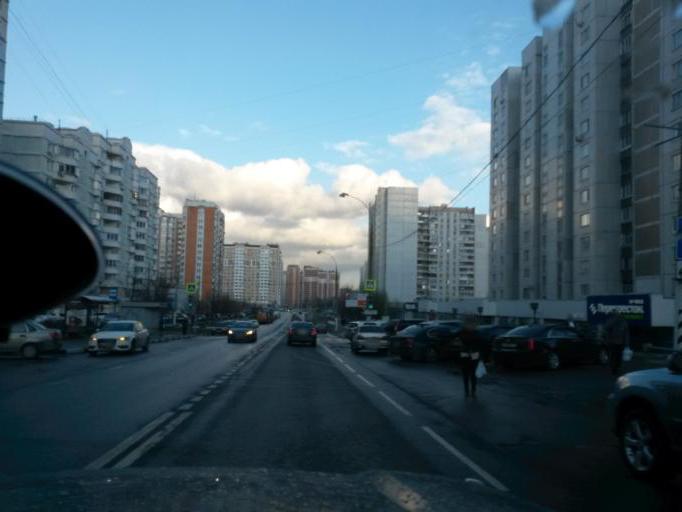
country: RU
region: Moscow
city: Annino
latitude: 55.5678
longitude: 37.5688
